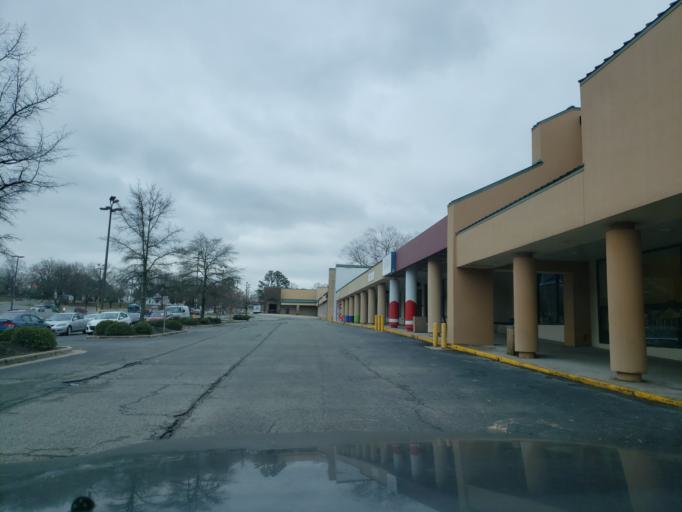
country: US
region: North Carolina
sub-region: Durham County
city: Durham
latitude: 35.9892
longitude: -78.9277
